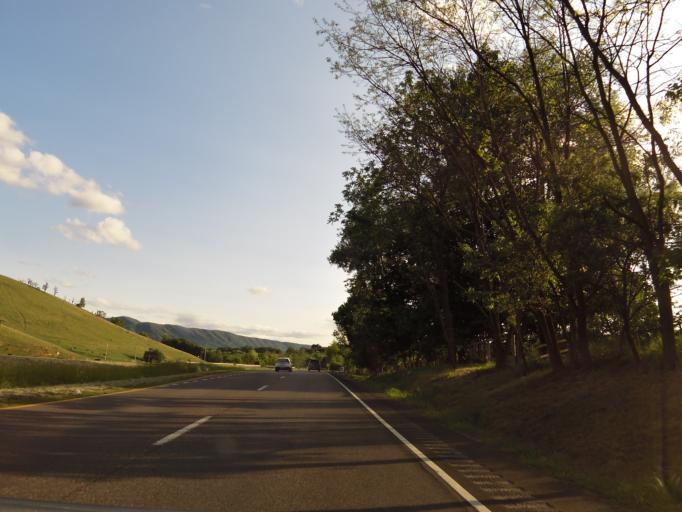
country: US
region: Virginia
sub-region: Russell County
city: Honaker
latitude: 36.9419
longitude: -81.9618
